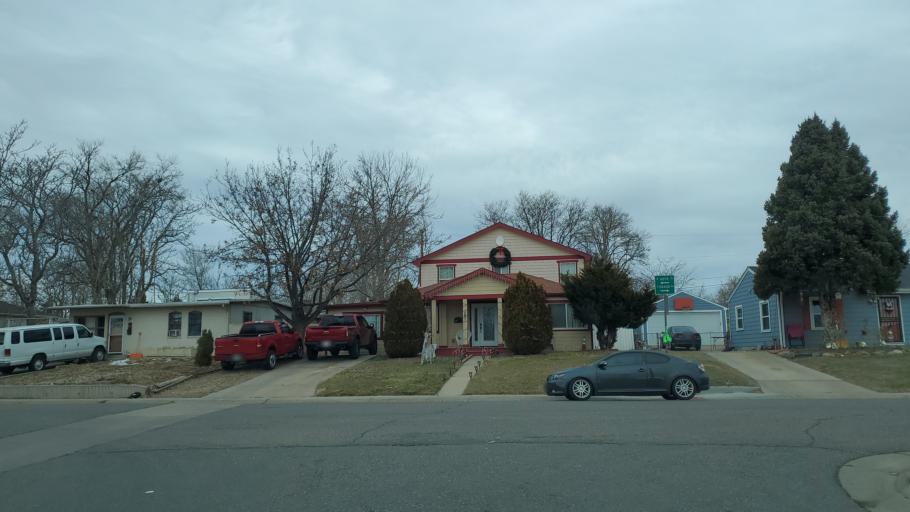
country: US
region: Colorado
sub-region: Denver County
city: Denver
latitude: 39.6975
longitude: -105.0043
